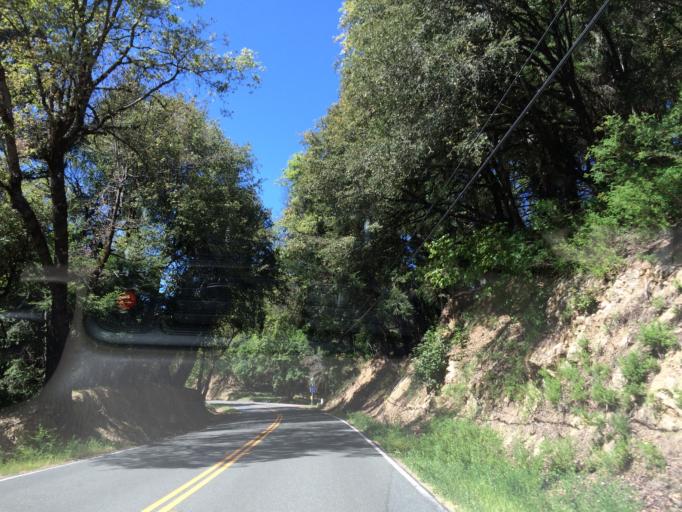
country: US
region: California
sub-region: Santa Clara County
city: Saratoga
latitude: 37.2159
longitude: -122.0692
